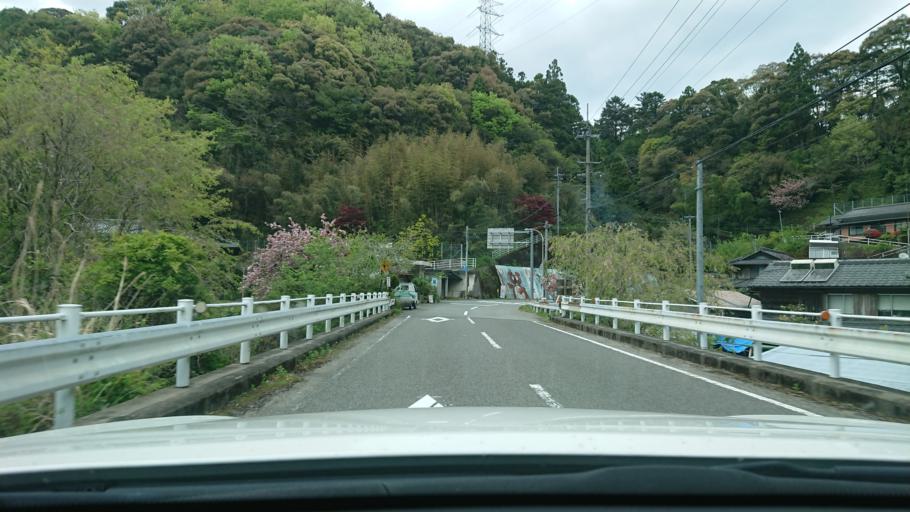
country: JP
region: Tokushima
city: Ishii
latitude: 33.9151
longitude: 134.4214
